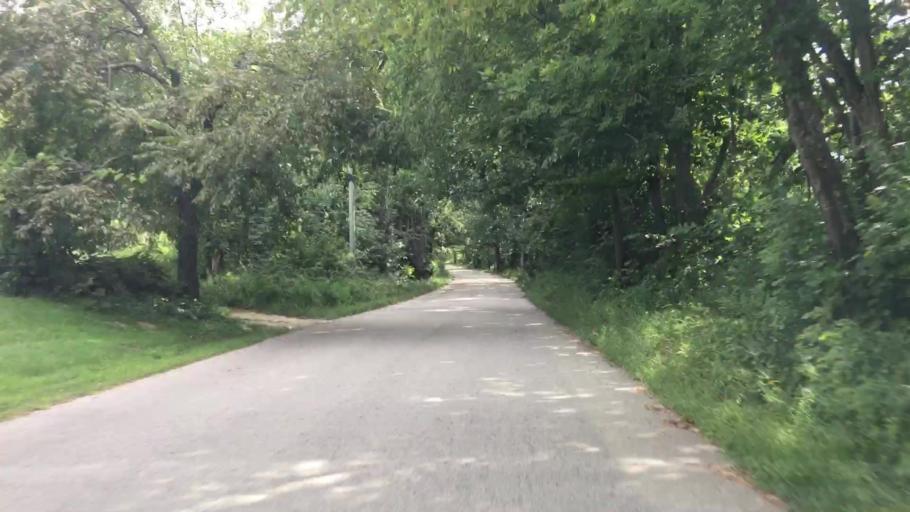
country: US
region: New Hampshire
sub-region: Strafford County
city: Madbury
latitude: 43.1667
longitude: -70.9157
